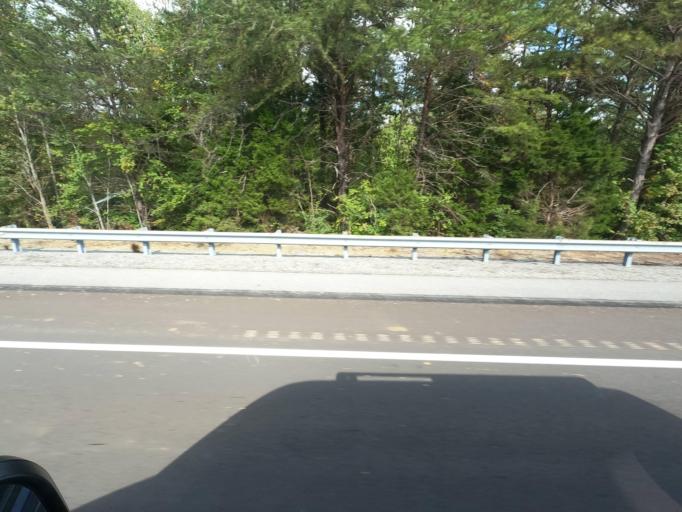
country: US
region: Tennessee
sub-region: Loudon County
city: Lenoir City
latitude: 35.8480
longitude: -84.3211
